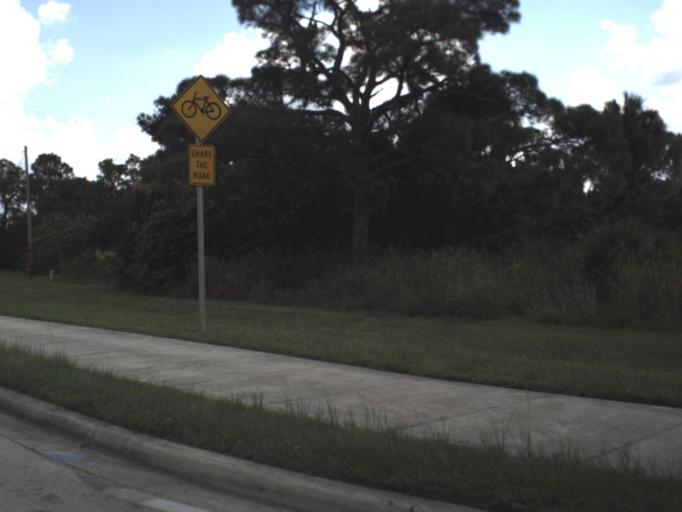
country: US
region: Florida
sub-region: Lee County
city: Tice
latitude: 26.7150
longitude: -81.8188
